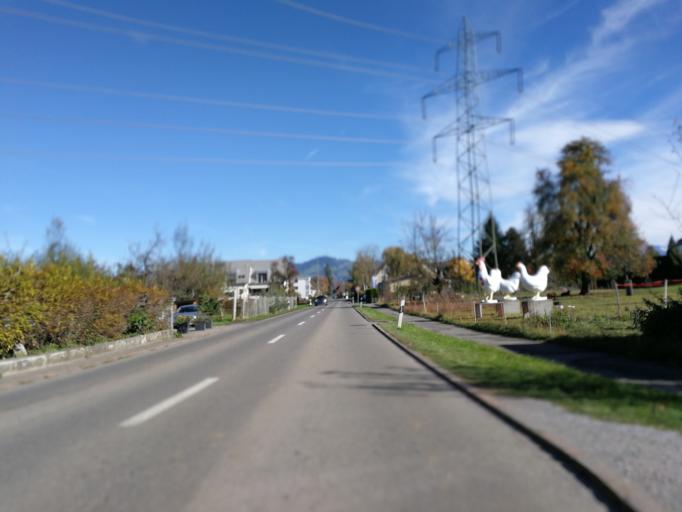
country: CH
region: Zurich
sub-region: Bezirk Hinwil
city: Binzikon
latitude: 47.2757
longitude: 8.7518
